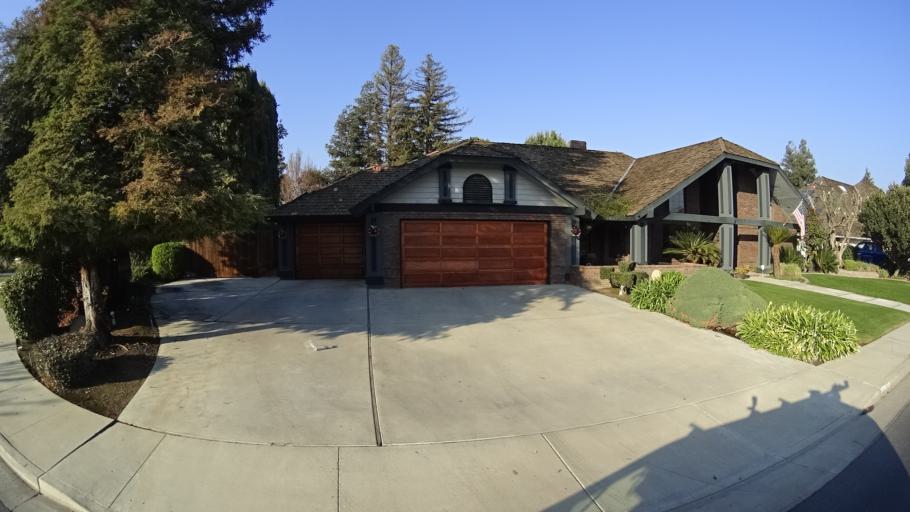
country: US
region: California
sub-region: Kern County
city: Greenacres
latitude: 35.3370
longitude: -119.1036
